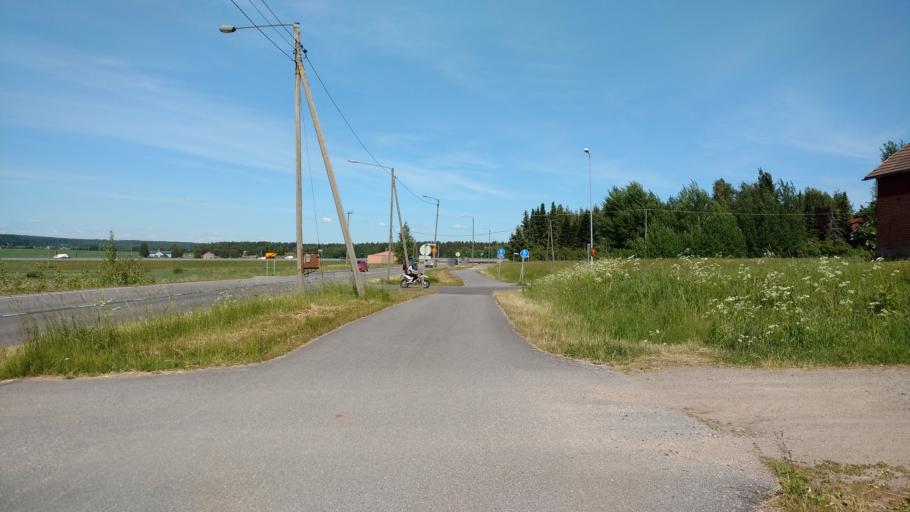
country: FI
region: Varsinais-Suomi
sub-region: Salo
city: Salo
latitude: 60.4097
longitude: 23.1854
